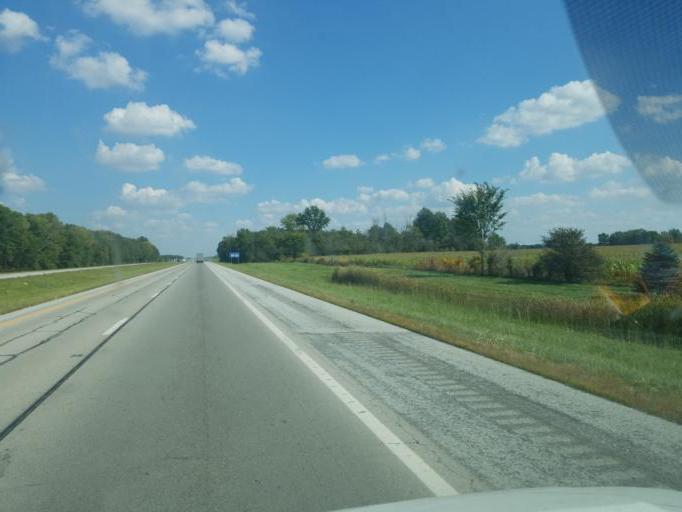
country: US
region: Ohio
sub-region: Allen County
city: Lima
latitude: 40.8240
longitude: -84.1120
